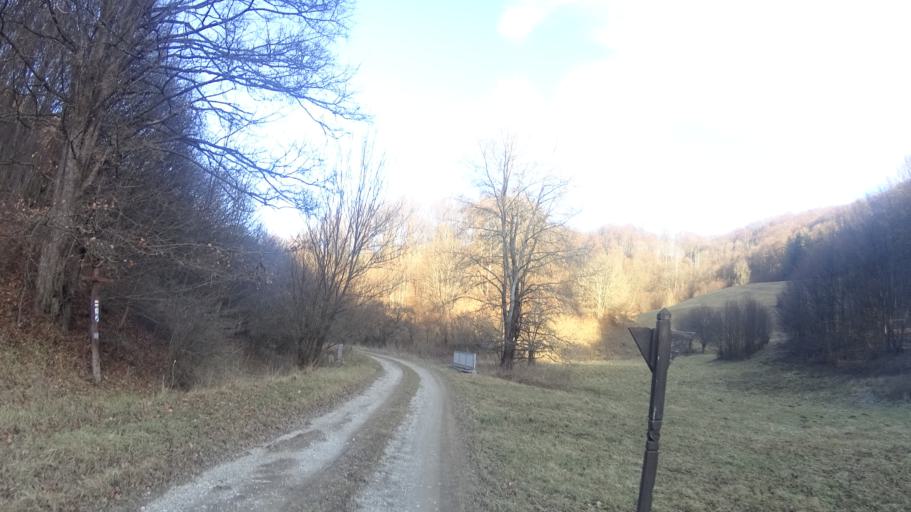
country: HU
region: Borsod-Abauj-Zemplen
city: Saly
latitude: 48.0410
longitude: 20.5649
